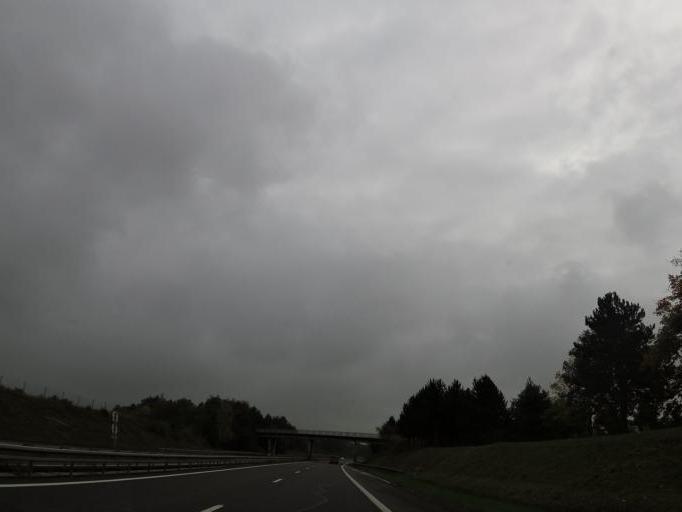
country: FR
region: Champagne-Ardenne
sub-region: Departement de la Marne
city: Fagnieres
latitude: 49.0402
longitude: 4.3389
